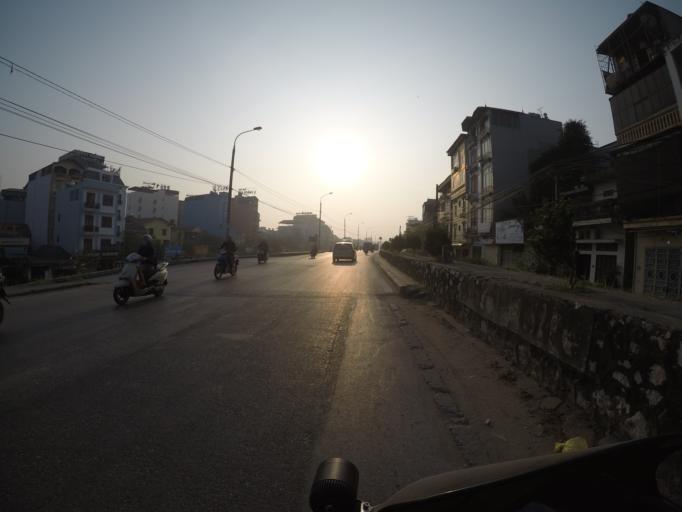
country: VN
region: Ha Noi
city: Hoan Kiem
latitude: 21.0390
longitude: 105.8667
